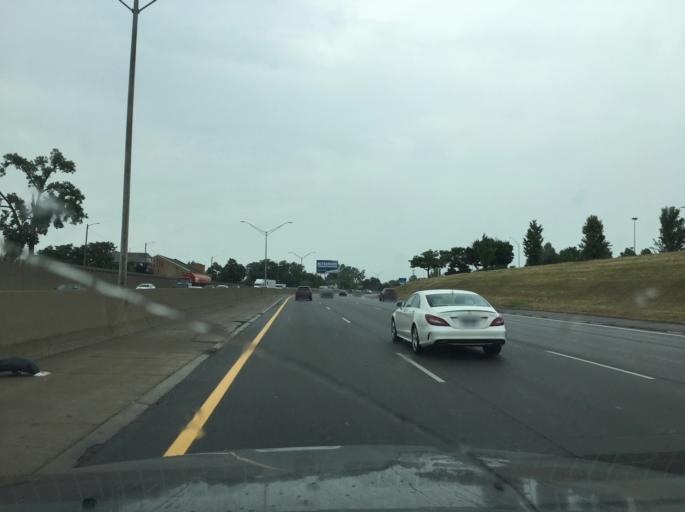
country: US
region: Michigan
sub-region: Wayne County
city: Hamtramck
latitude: 42.3872
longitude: -83.0686
